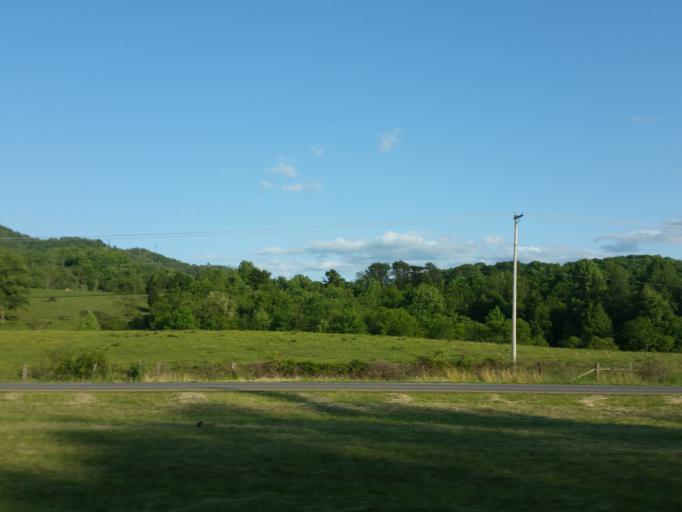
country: US
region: Virginia
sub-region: Russell County
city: Lebanon
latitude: 36.8460
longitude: -82.1296
